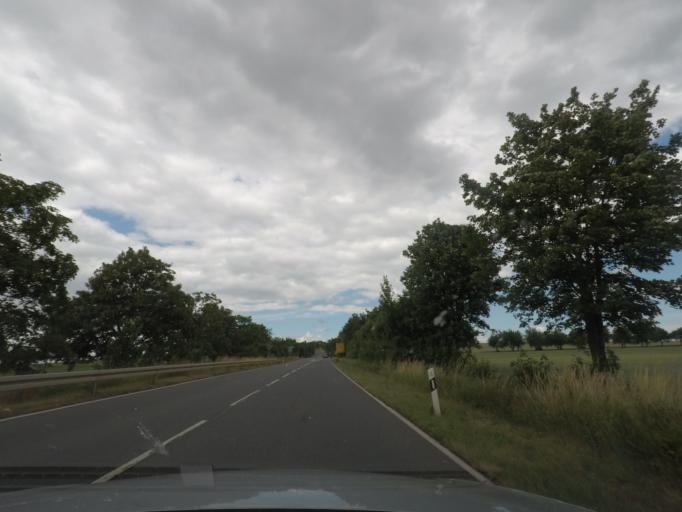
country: DE
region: Saxony-Anhalt
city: Volpke
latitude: 52.1024
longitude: 11.0768
